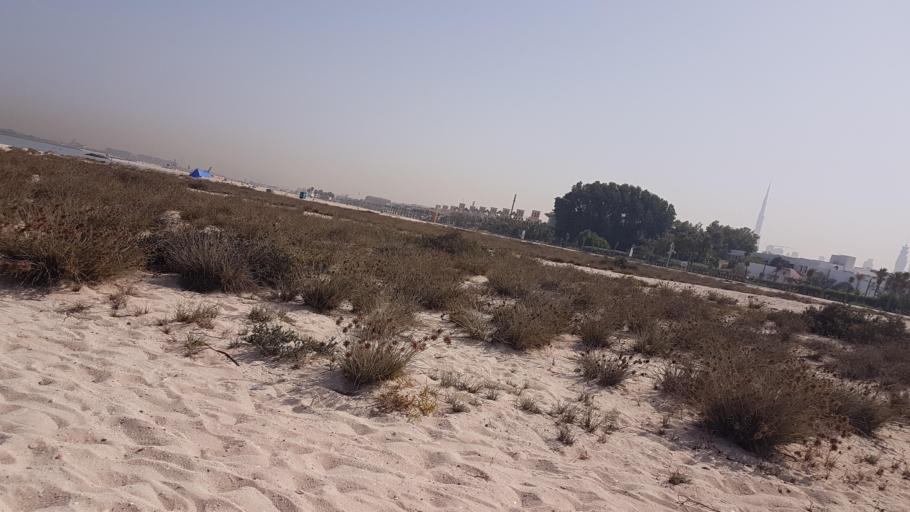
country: AE
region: Dubai
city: Dubai
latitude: 25.1797
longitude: 55.2199
